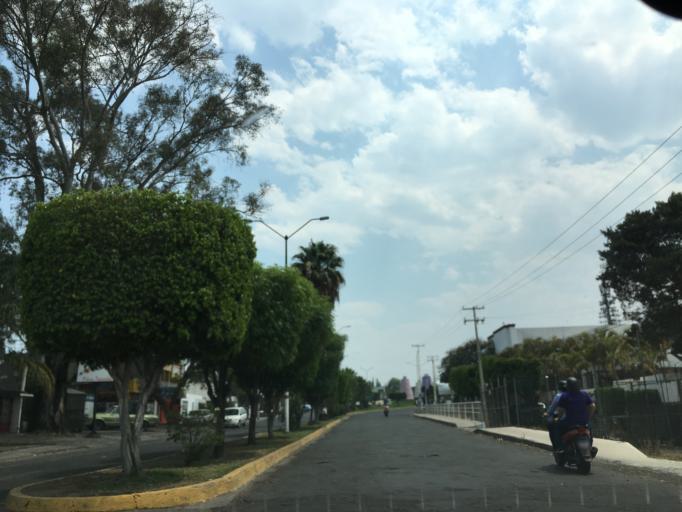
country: MX
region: Guanajuato
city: Moroleon
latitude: 20.1275
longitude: -101.1802
